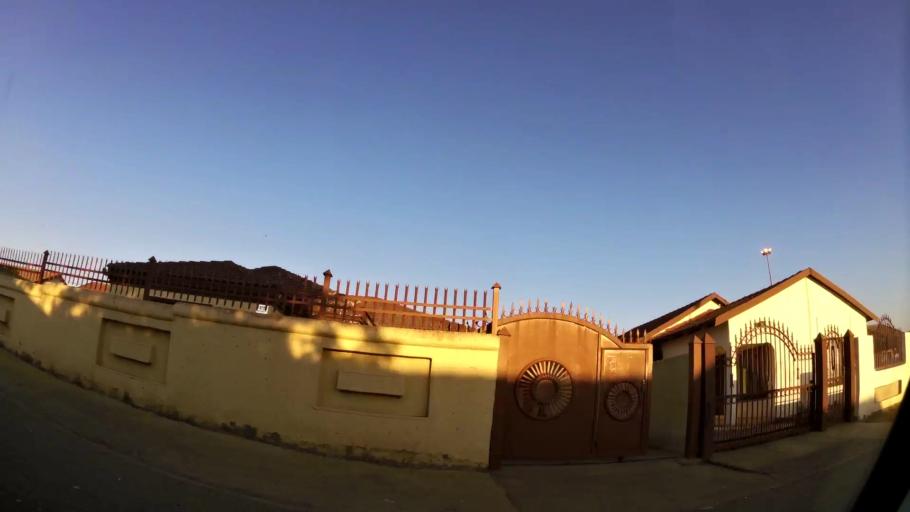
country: ZA
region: Gauteng
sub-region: City of Tshwane Metropolitan Municipality
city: Cullinan
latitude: -25.7204
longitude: 28.3896
